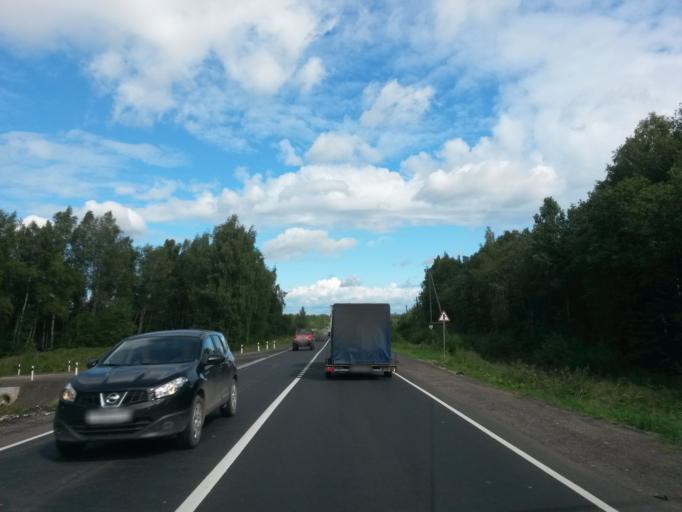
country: RU
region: Jaroslavl
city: Yaroslavl
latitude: 57.5047
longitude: 39.8985
